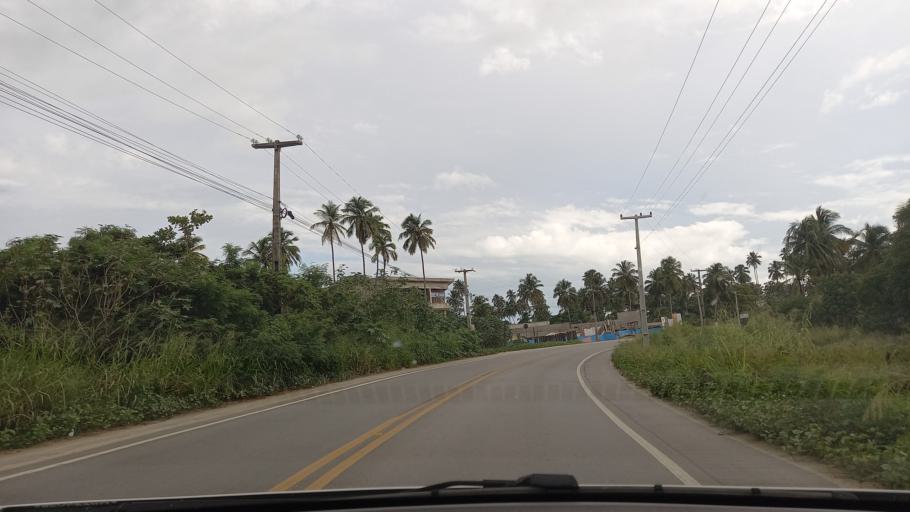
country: BR
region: Alagoas
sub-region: Maragogi
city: Maragogi
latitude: -8.9774
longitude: -35.1848
